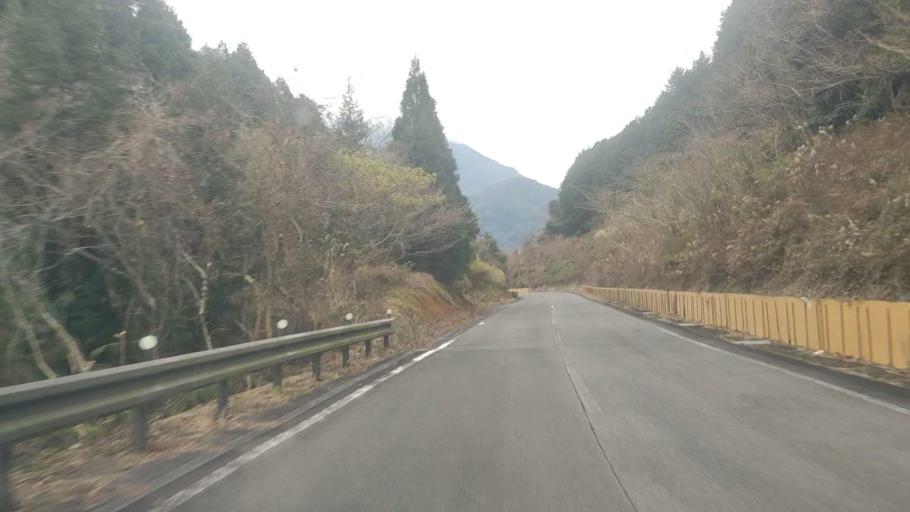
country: JP
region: Nagasaki
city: Shimabara
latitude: 32.7880
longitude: 130.2834
